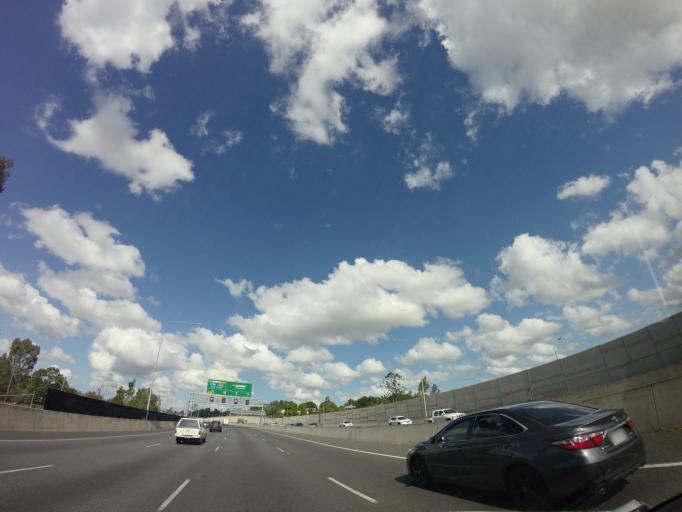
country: AU
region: Queensland
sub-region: Ipswich
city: Goodna
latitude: -27.6090
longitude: 152.9073
